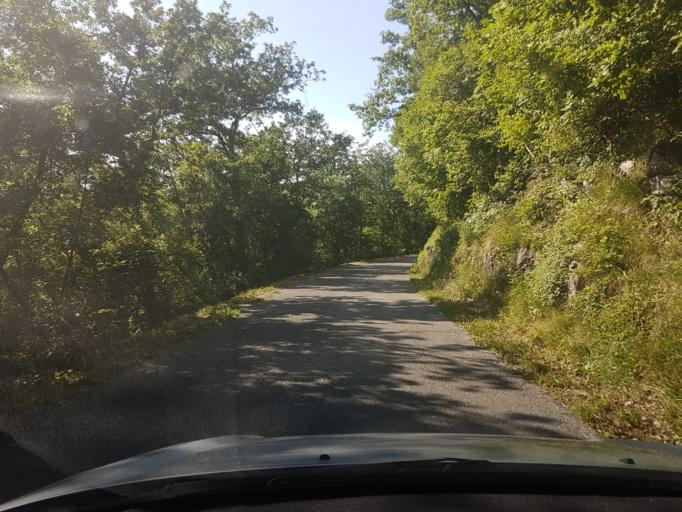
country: SI
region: Divaca
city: Divaca
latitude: 45.7464
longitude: 13.9988
